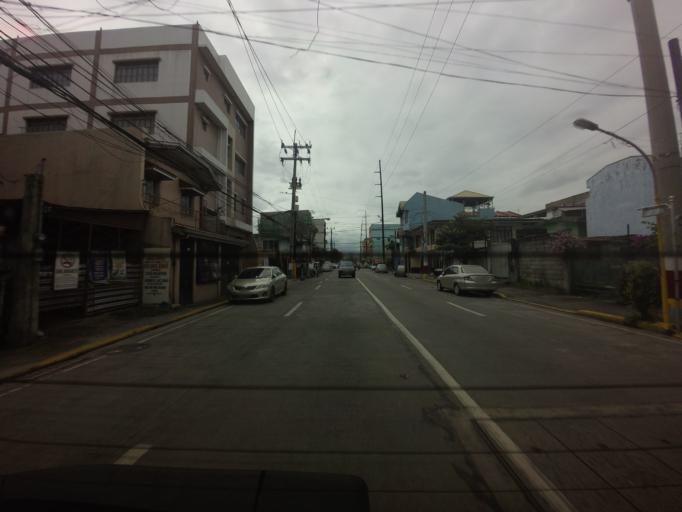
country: PH
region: Metro Manila
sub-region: City of Manila
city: Manila
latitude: 14.6268
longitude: 120.9680
